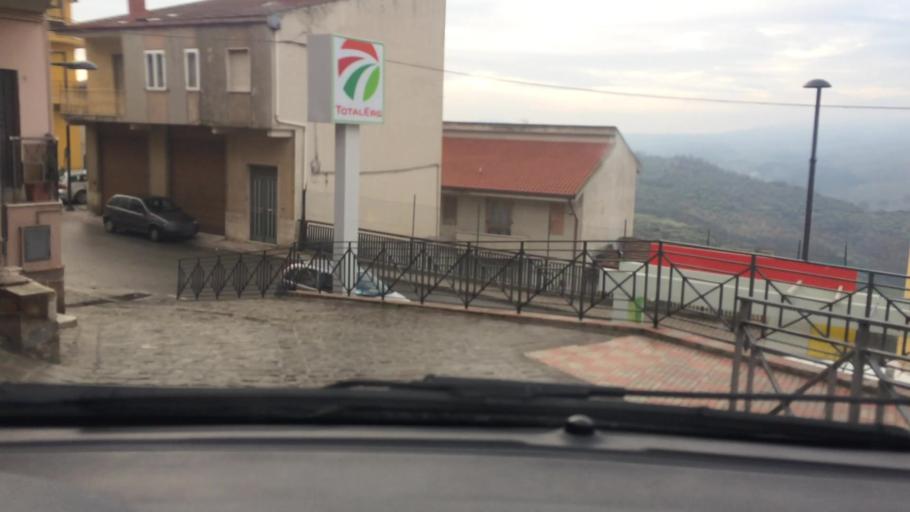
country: IT
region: Basilicate
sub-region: Provincia di Matera
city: San Mauro Forte
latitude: 40.4869
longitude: 16.2474
